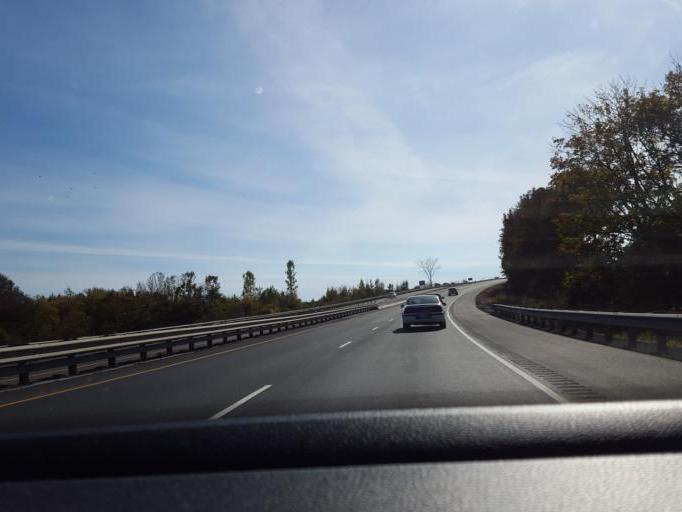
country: CA
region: Ontario
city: Oshawa
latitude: 43.9269
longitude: -78.6003
